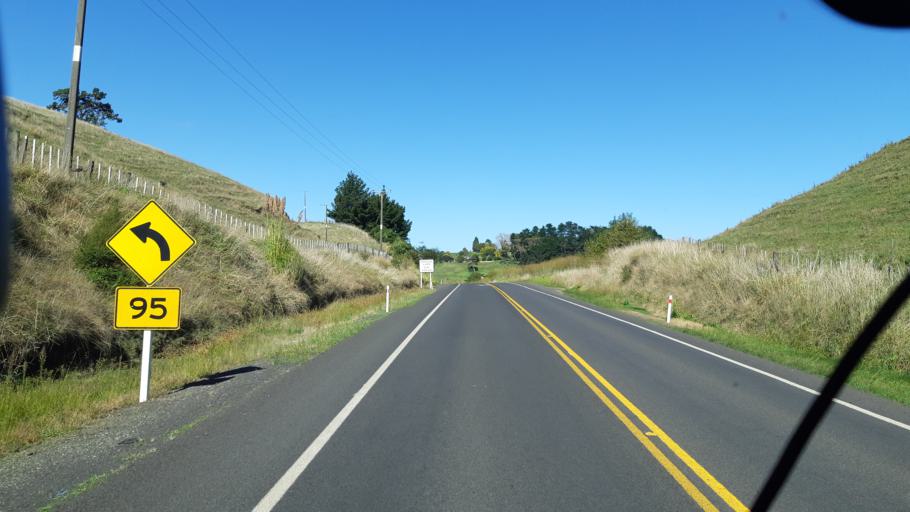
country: NZ
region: Manawatu-Wanganui
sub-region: Wanganui District
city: Wanganui
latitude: -39.9633
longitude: 175.1004
